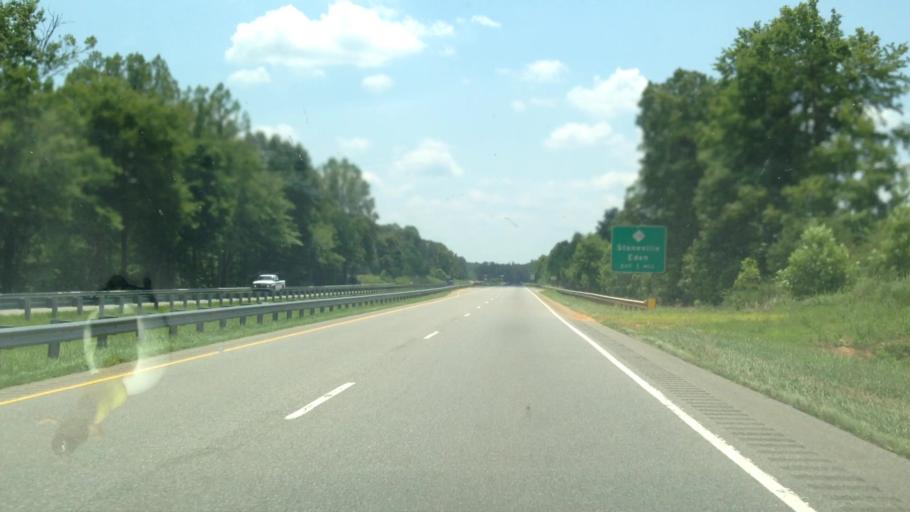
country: US
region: North Carolina
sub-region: Rockingham County
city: Stoneville
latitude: 36.4870
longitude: -79.9253
